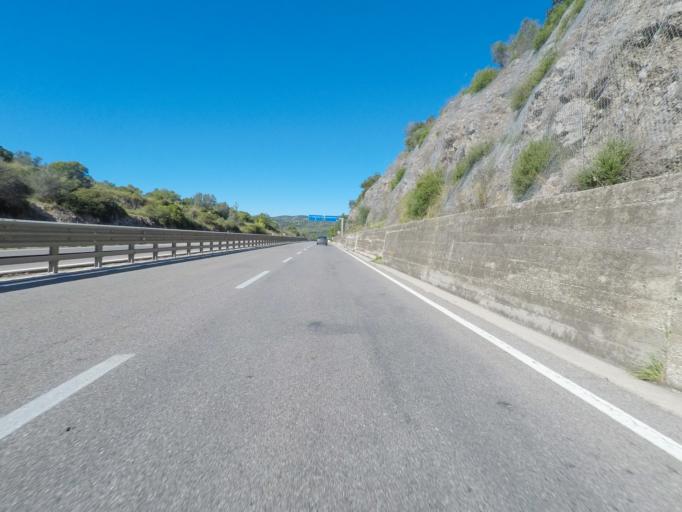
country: IT
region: Tuscany
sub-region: Provincia di Grosseto
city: Orbetello Scalo
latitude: 42.4257
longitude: 11.2876
